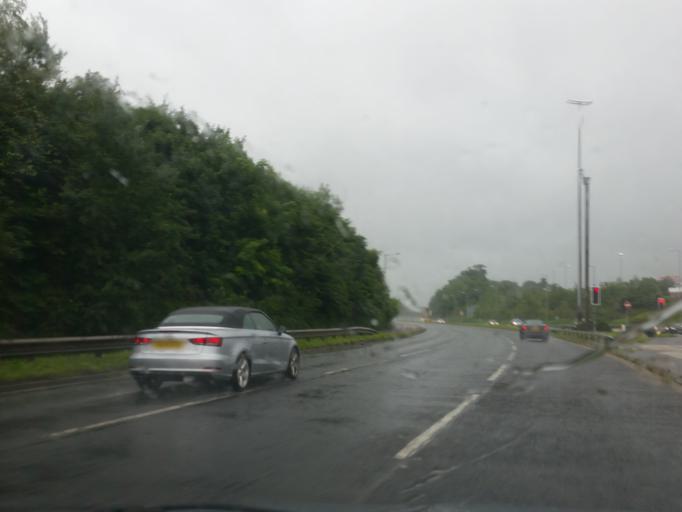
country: GB
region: Northern Ireland
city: Holywood
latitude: 54.6187
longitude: -5.8616
